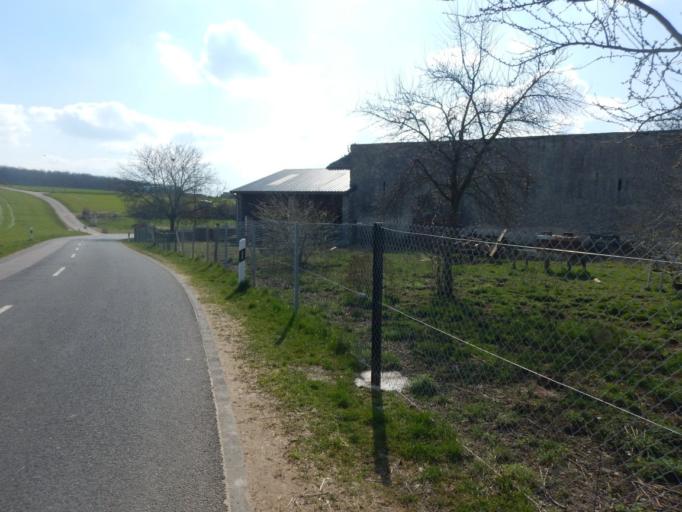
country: LU
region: Grevenmacher
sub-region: Canton d'Echternach
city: Beaufort
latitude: 49.8183
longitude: 6.2727
